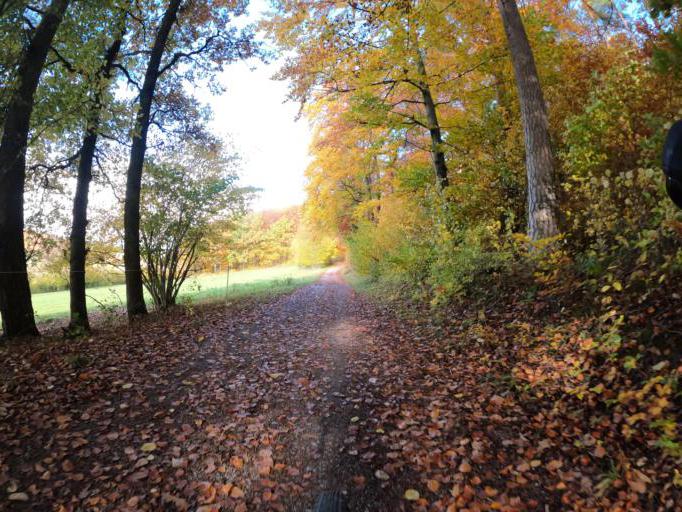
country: DE
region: Baden-Wuerttemberg
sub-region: Regierungsbezirk Stuttgart
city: Aidlingen
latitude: 48.7038
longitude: 8.9012
